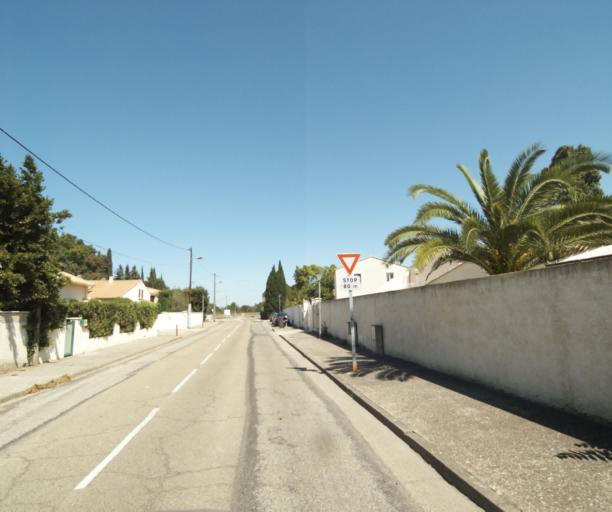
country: FR
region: Languedoc-Roussillon
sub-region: Departement du Gard
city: Rodilhan
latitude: 43.8314
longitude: 4.4321
